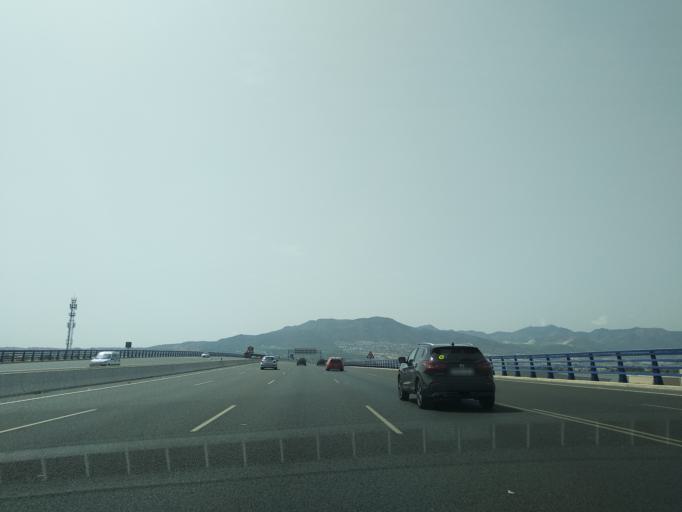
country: ES
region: Andalusia
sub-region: Provincia de Malaga
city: Alhaurin de la Torre
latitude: 36.7052
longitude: -4.5144
